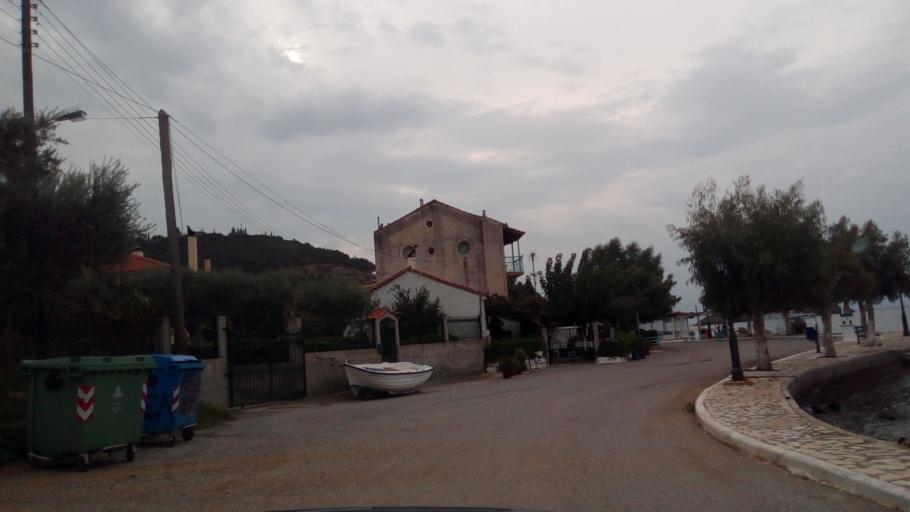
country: GR
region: West Greece
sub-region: Nomos Achaias
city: Temeni
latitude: 38.3486
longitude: 22.1584
